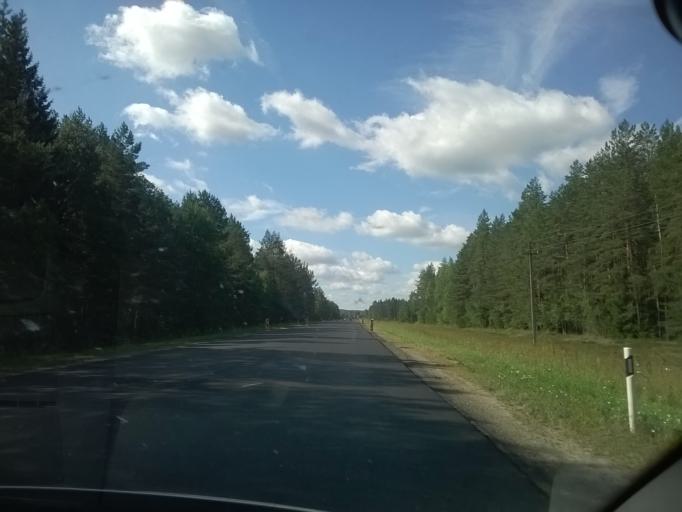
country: EE
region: Vorumaa
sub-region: Voru linn
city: Voru
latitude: 57.8045
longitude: 26.9653
